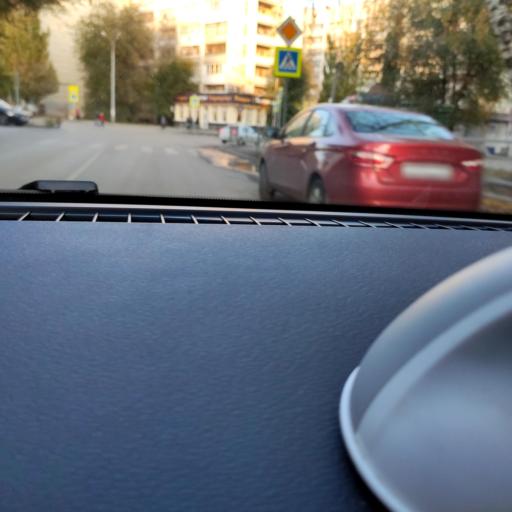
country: RU
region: Samara
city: Petra-Dubrava
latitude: 53.2344
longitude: 50.2718
